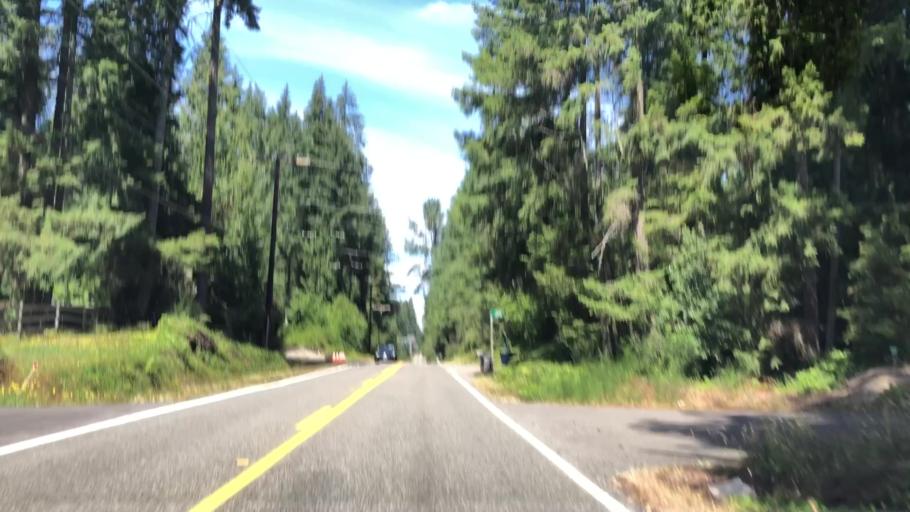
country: US
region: Washington
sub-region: Snohomish County
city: North Creek
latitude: 47.8256
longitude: -122.1643
